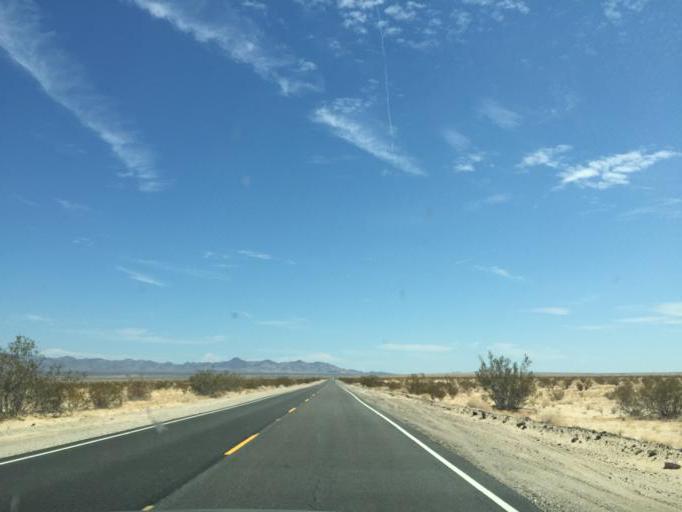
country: US
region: California
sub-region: Riverside County
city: Mesa Verde
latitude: 34.0979
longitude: -115.0202
